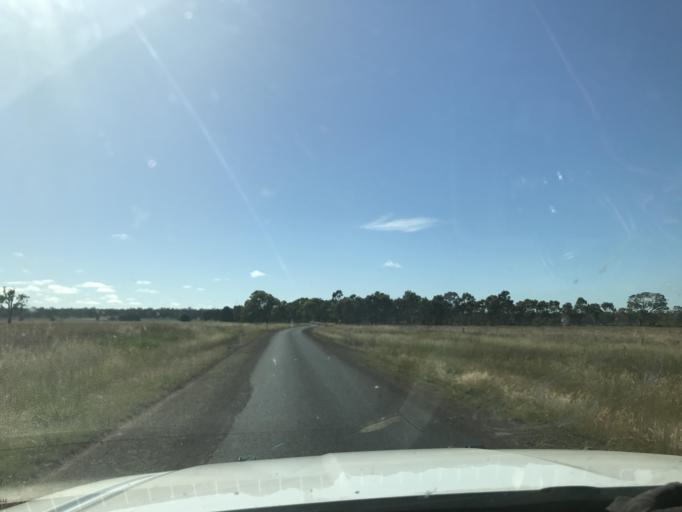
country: AU
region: Victoria
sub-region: Horsham
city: Horsham
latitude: -37.0860
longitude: 141.7543
